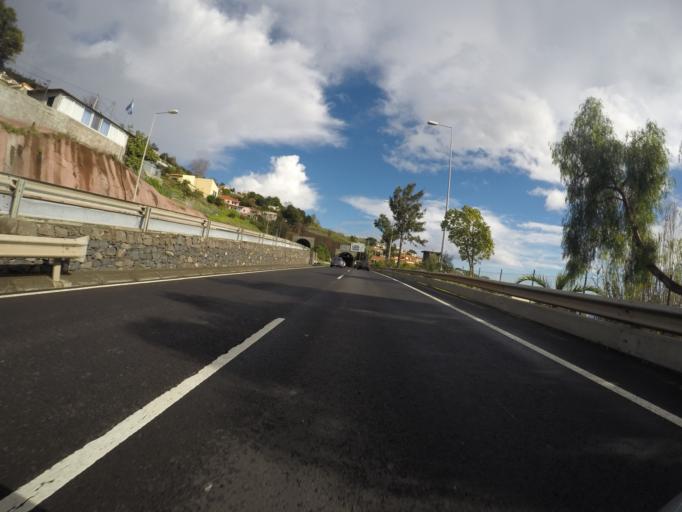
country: PT
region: Madeira
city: Canico
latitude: 32.6492
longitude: -16.8736
